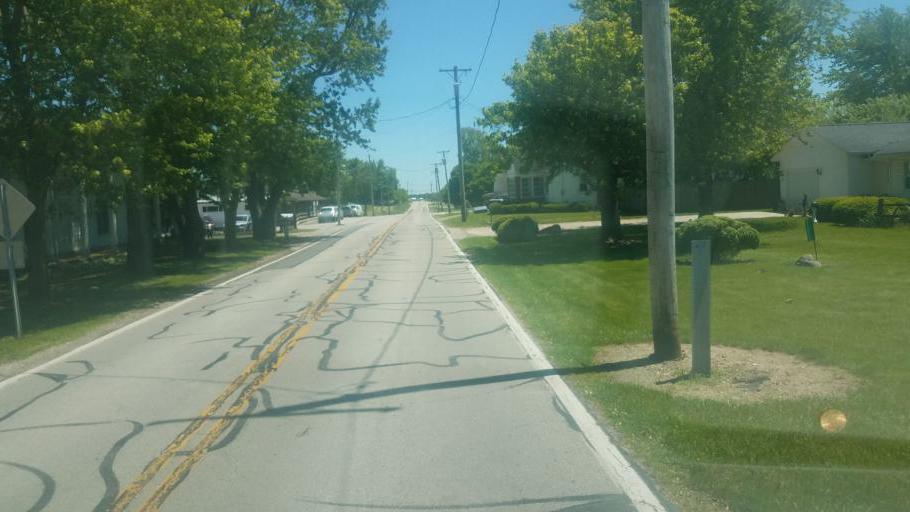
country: US
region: Ohio
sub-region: Darke County
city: Versailles
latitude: 40.2460
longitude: -84.5227
